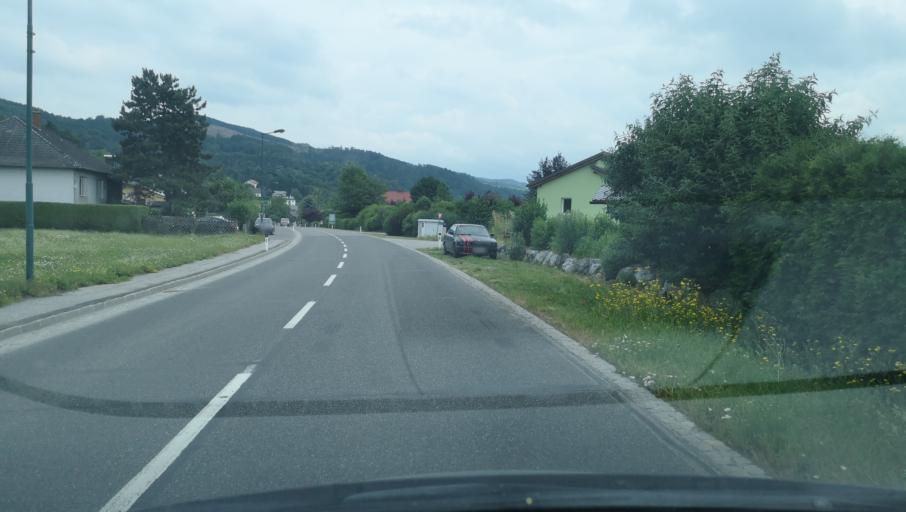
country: AT
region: Lower Austria
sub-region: Politischer Bezirk Melk
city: Ybbs an der Donau
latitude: 48.1927
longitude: 15.1043
